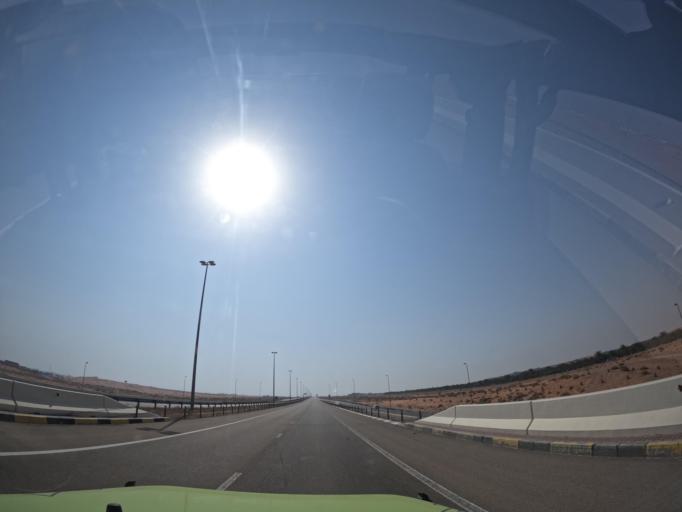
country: OM
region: Al Buraimi
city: Al Buraymi
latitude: 24.4082
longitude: 55.7048
